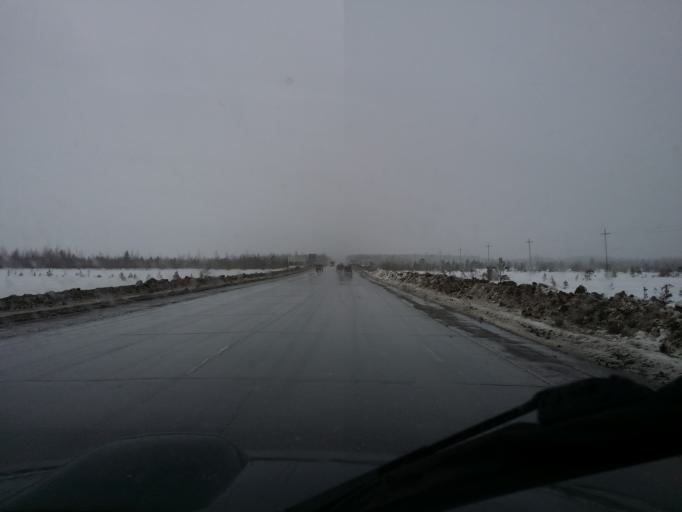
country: RU
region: Khanty-Mansiyskiy Avtonomnyy Okrug
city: Nizhnevartovsk
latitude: 60.9571
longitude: 76.7230
